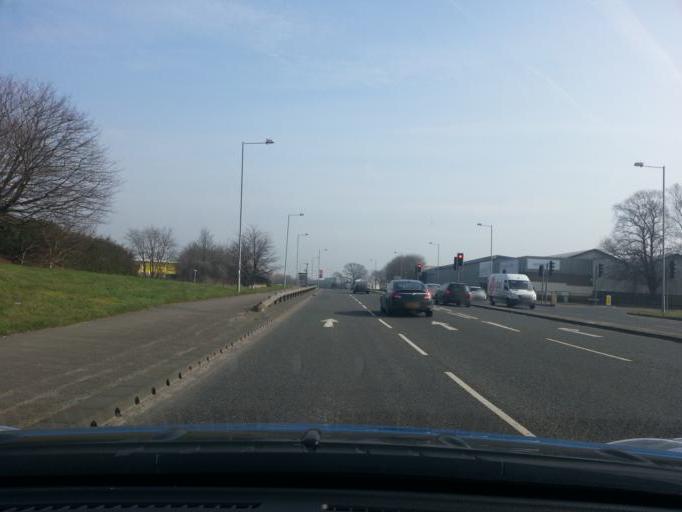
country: GB
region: England
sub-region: Borough of Swindon
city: Swindon
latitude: 51.5666
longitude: -1.7579
